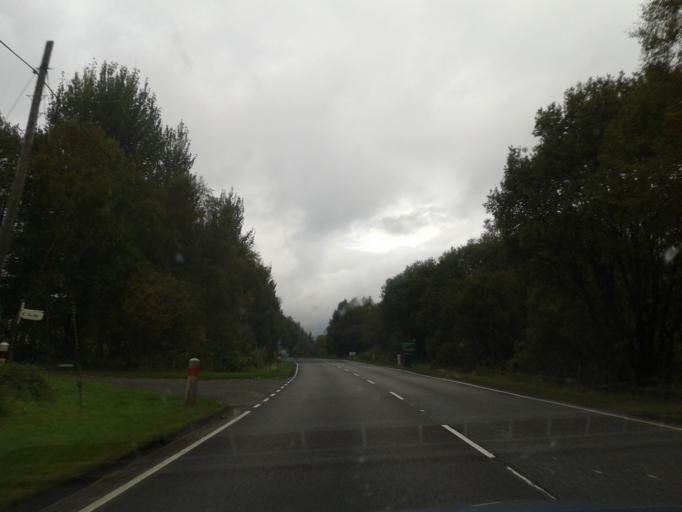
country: GB
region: Scotland
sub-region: Argyll and Bute
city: Garelochhead
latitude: 56.4161
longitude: -4.6654
